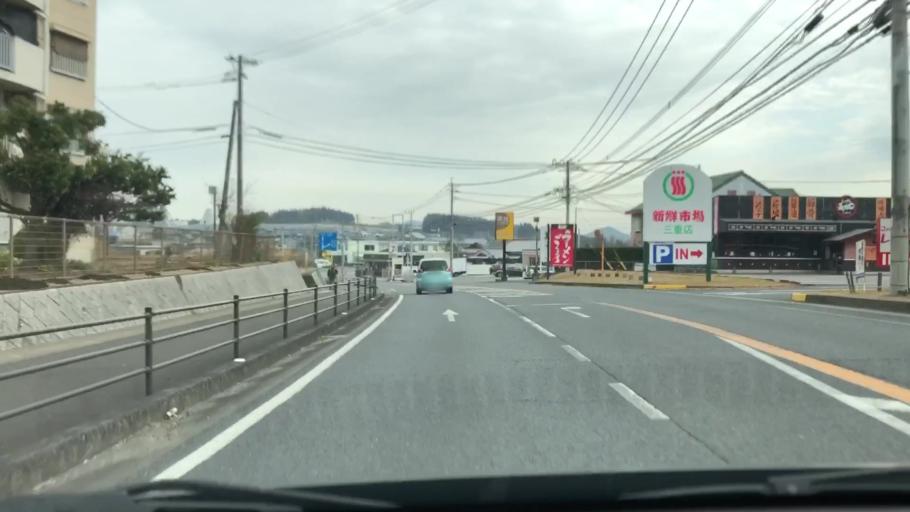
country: JP
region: Oita
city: Takedamachi
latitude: 32.9948
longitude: 131.6153
